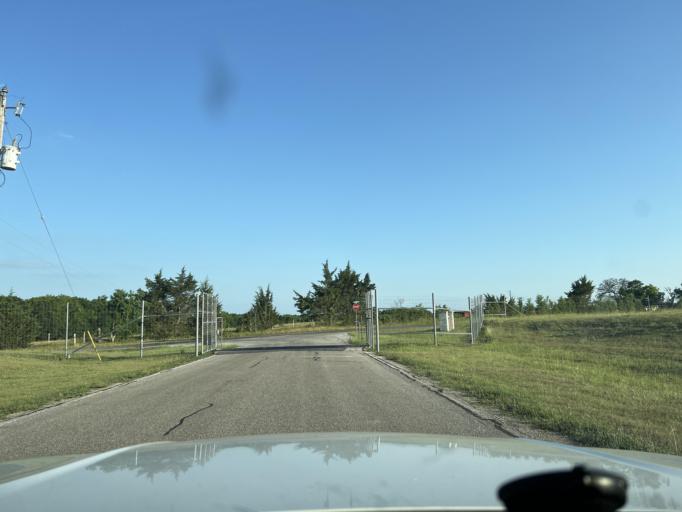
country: US
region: Texas
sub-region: Washington County
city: Brenham
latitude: 30.2112
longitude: -96.3707
